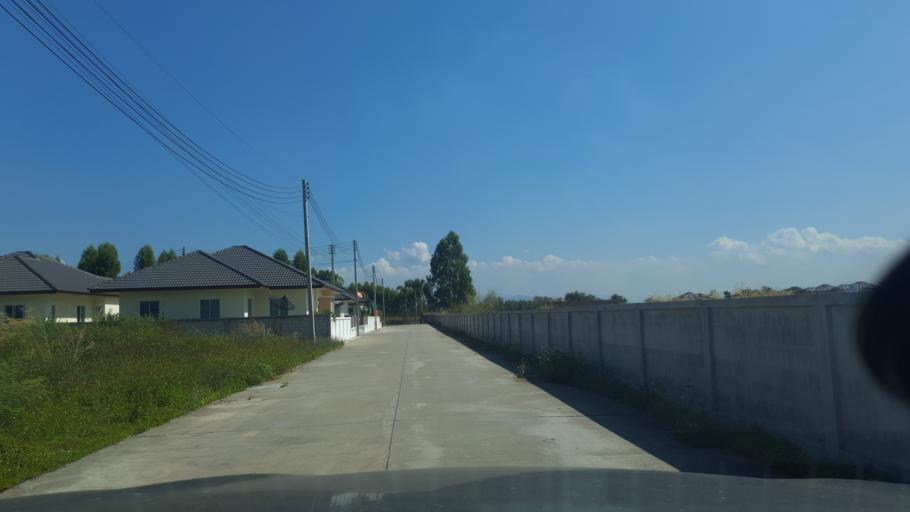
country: TH
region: Chiang Mai
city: San Sai
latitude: 18.8181
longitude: 99.0791
